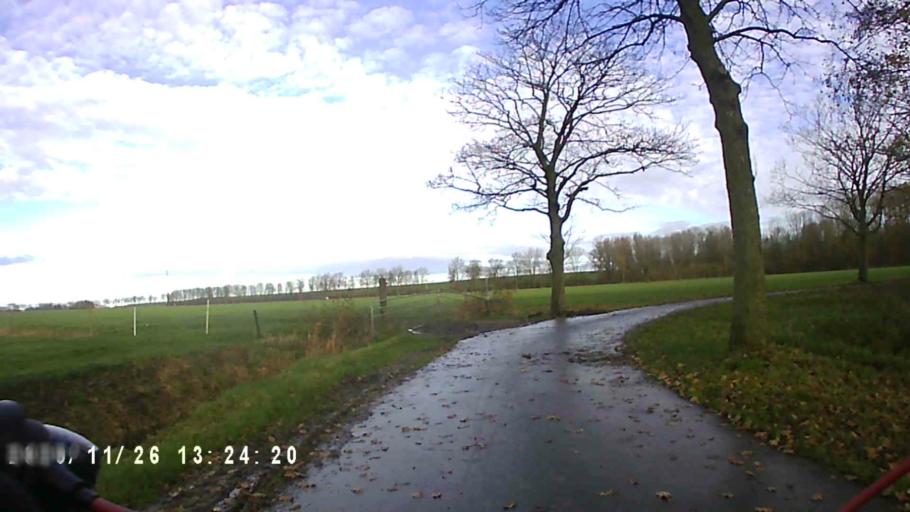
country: NL
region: Groningen
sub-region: Gemeente Delfzijl
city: Delfzijl
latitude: 53.3445
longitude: 6.8985
